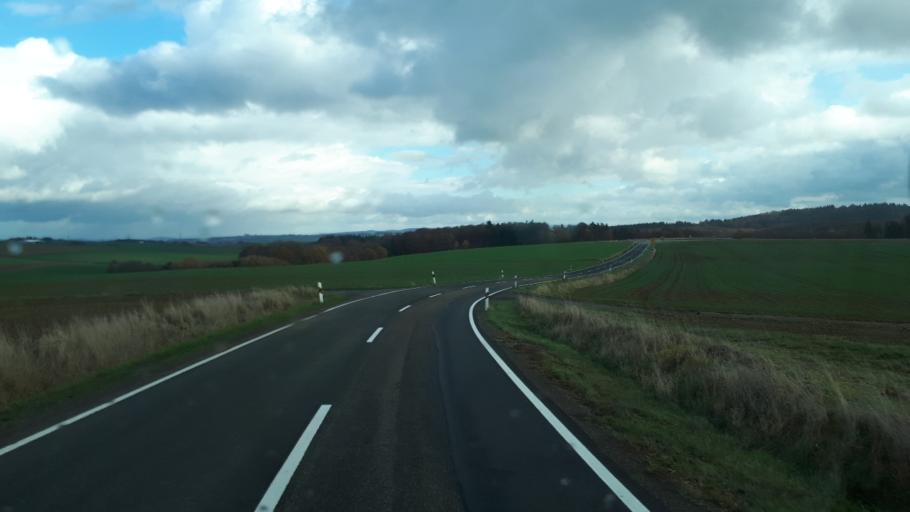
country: DE
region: Rheinland-Pfalz
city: Brohl
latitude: 50.2082
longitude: 7.2707
